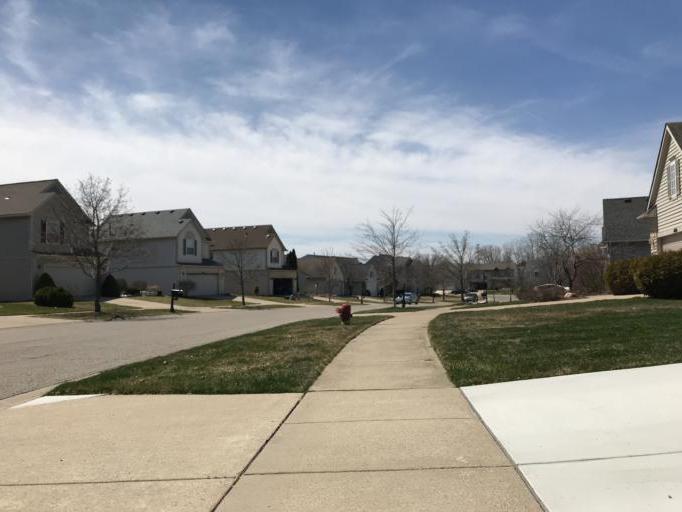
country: US
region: Michigan
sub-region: Washtenaw County
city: Ann Arbor
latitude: 42.2610
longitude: -83.7867
